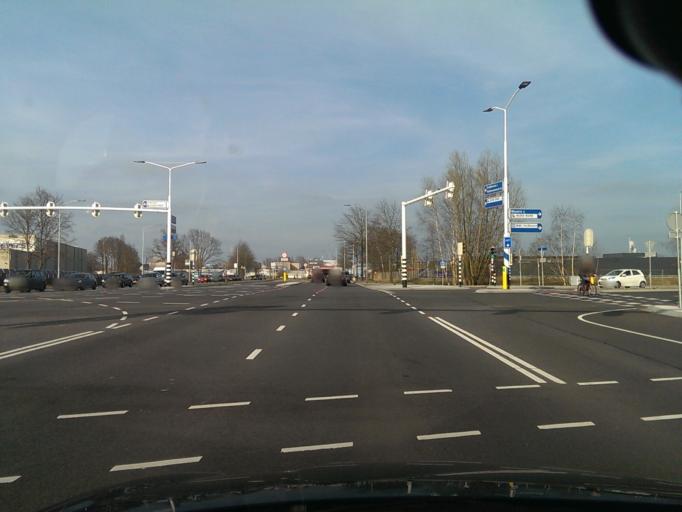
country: NL
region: North Brabant
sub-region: Gemeente Veldhoven
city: Veldhoven
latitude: 51.4082
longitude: 5.4176
